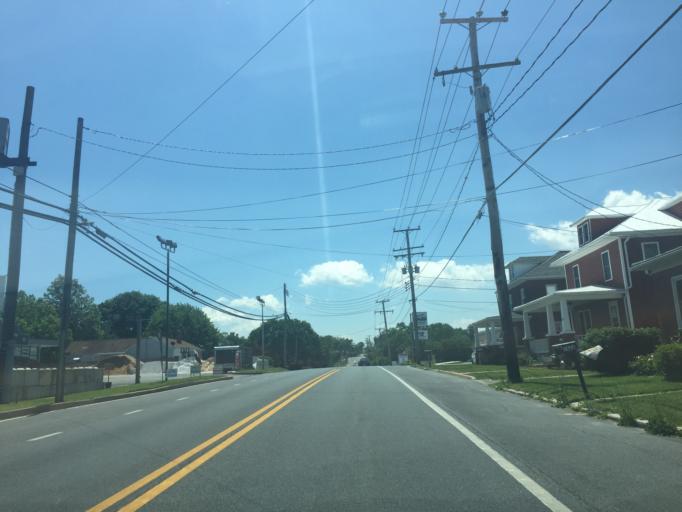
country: US
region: Maryland
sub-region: Carroll County
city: Hampstead
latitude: 39.6199
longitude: -76.8571
